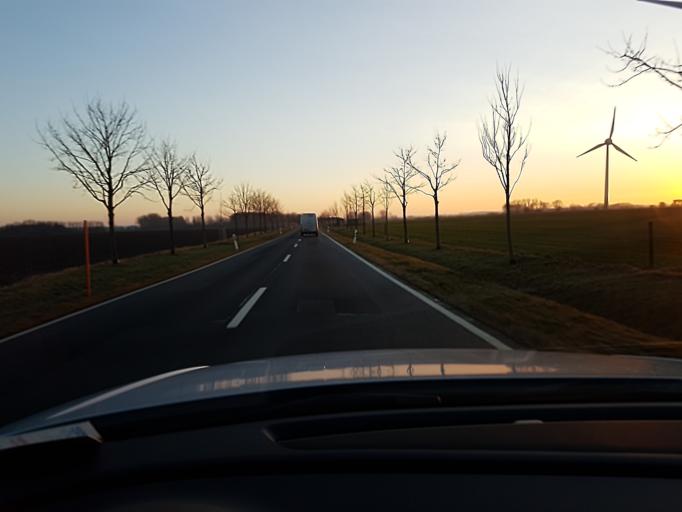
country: DE
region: Mecklenburg-Vorpommern
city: Wiek
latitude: 54.5959
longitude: 13.2899
